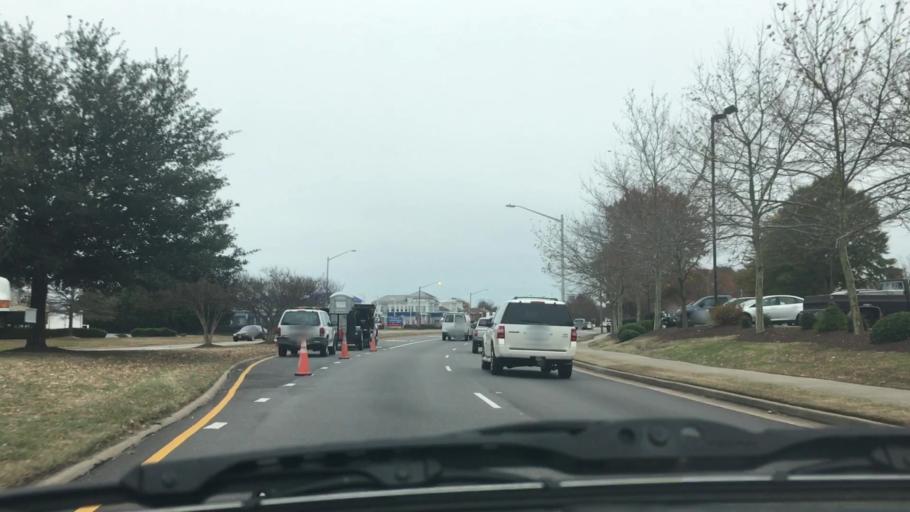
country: US
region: Virginia
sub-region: City of Chesapeake
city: Chesapeake
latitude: 36.8231
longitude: -76.1271
